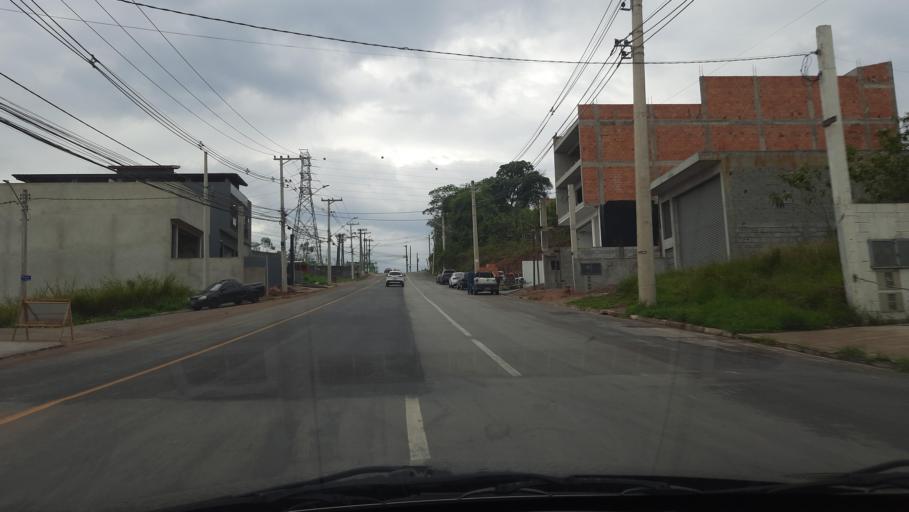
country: BR
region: Sao Paulo
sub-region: Caieiras
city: Caieiras
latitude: -23.3769
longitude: -46.6999
